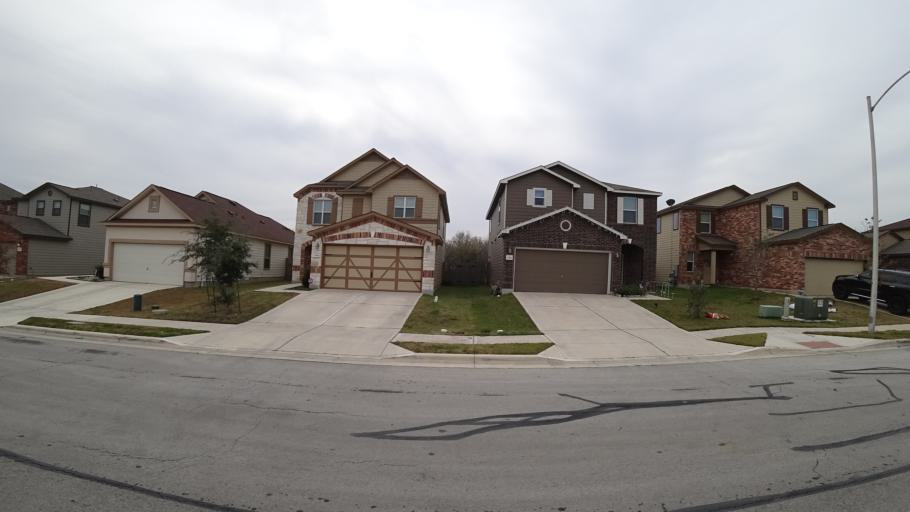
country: US
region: Texas
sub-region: Travis County
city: Onion Creek
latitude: 30.1471
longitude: -97.7421
